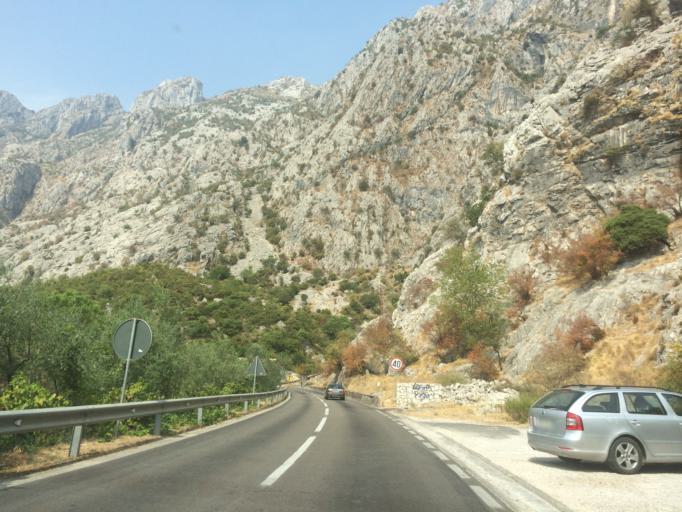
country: ME
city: Dobrota
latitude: 42.4848
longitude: 18.7663
